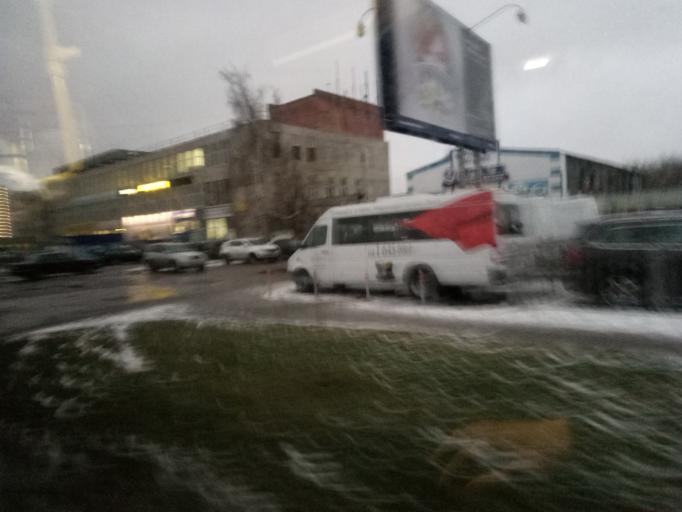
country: RU
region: Tula
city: Tula
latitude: 54.2085
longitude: 37.5740
